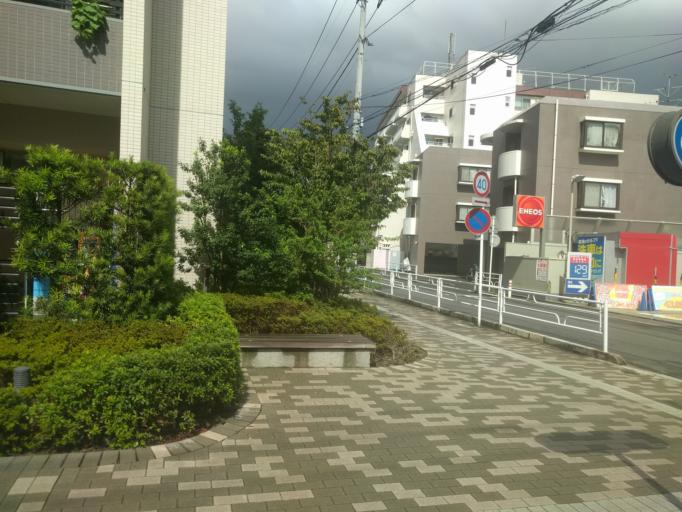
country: JP
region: Saitama
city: Shimotoda
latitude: 35.8298
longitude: 139.6804
